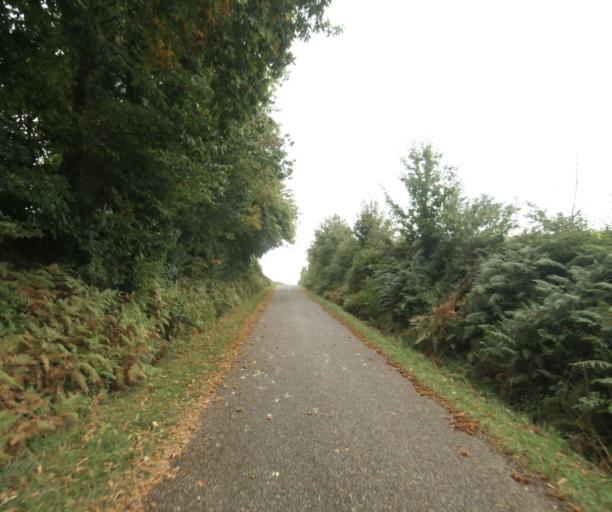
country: FR
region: Midi-Pyrenees
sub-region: Departement du Gers
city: Cazaubon
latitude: 43.8984
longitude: -0.1552
